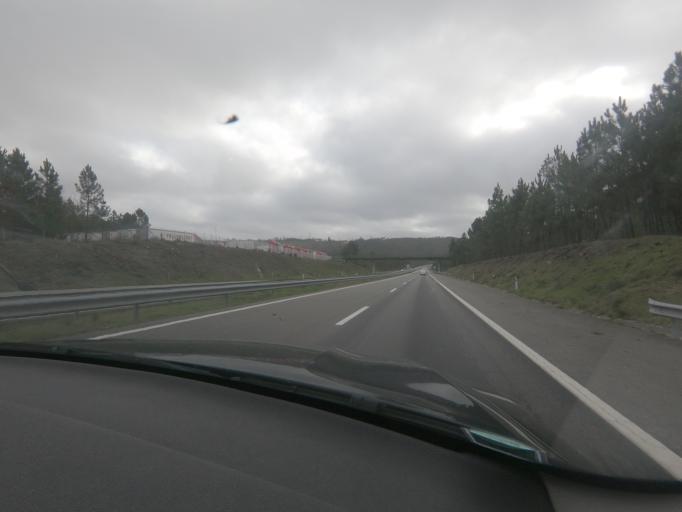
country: PT
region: Viseu
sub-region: Castro Daire
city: Castro Daire
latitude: 40.8520
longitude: -7.9278
